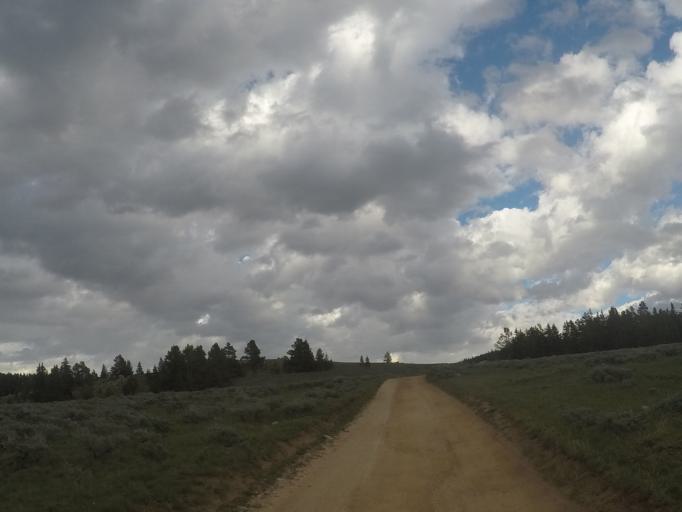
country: US
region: Wyoming
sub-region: Sheridan County
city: Sheridan
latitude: 44.5027
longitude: -107.4458
